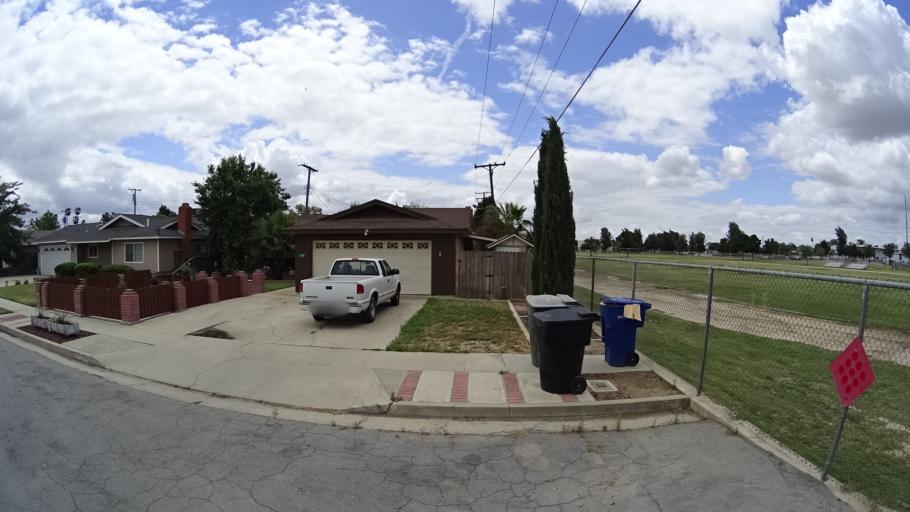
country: US
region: California
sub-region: Kings County
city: Hanford
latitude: 36.3396
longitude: -119.6279
